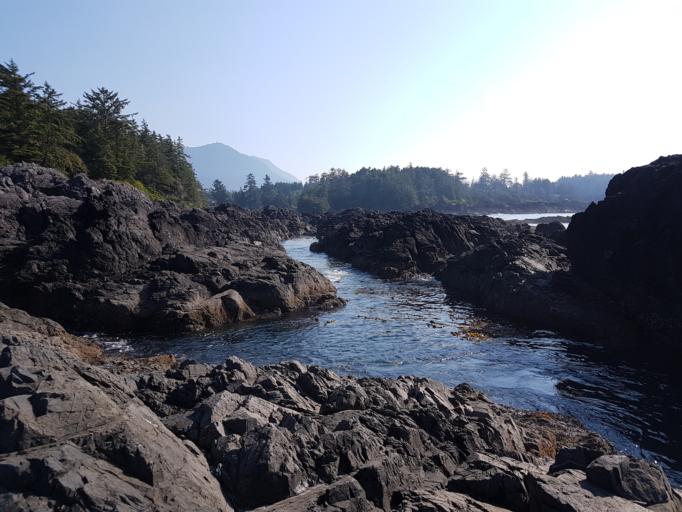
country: CA
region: British Columbia
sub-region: Regional District of Alberni-Clayoquot
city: Ucluelet
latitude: 48.9209
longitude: -125.5381
